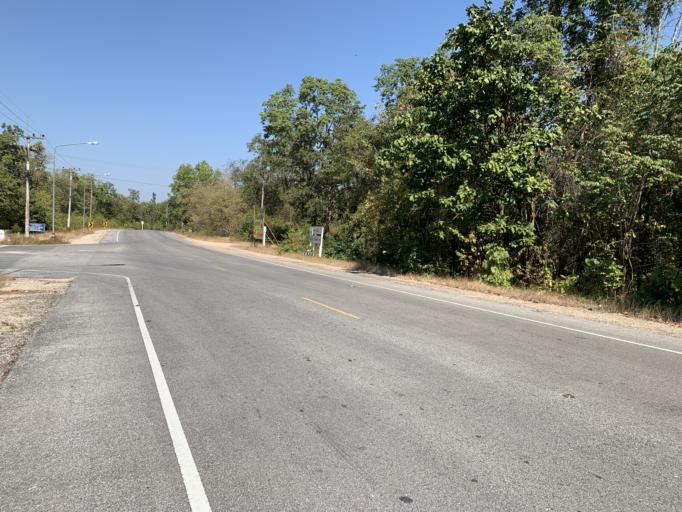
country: TH
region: Lampang
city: Mae Phrik
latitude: 17.4796
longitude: 99.1166
